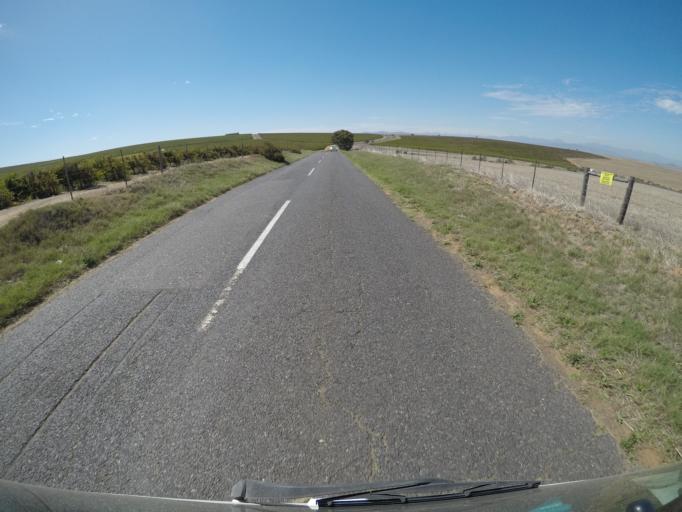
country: ZA
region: Western Cape
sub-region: City of Cape Town
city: Sunset Beach
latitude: -33.7203
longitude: 18.5753
